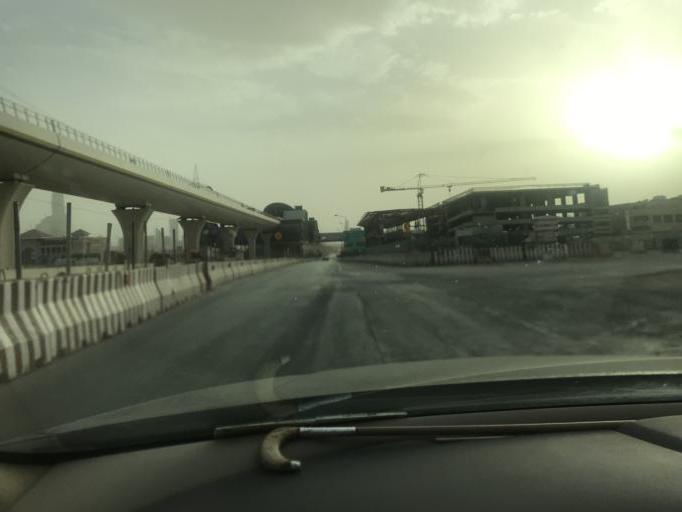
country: SA
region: Ar Riyad
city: Riyadh
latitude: 24.7877
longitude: 46.6628
